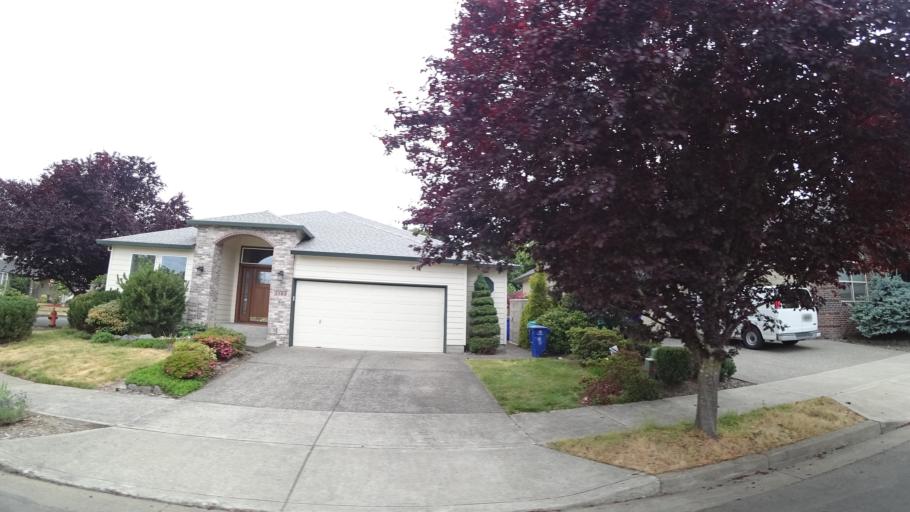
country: US
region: Washington
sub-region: Clark County
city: Vancouver
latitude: 45.5906
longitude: -122.6440
